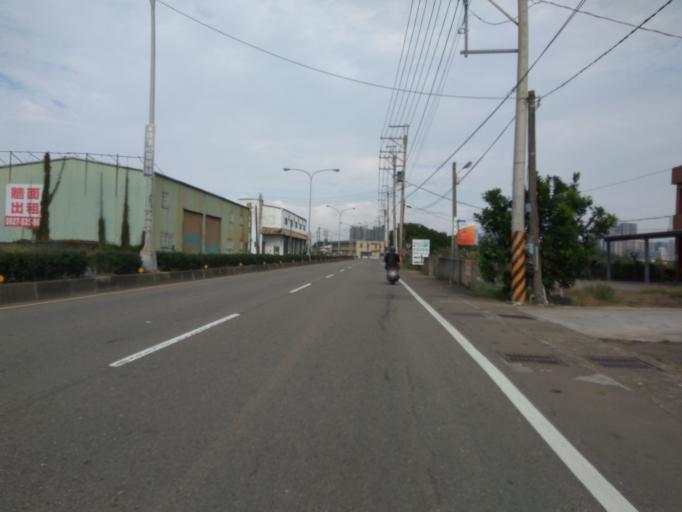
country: TW
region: Taiwan
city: Taoyuan City
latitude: 24.9977
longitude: 121.2188
